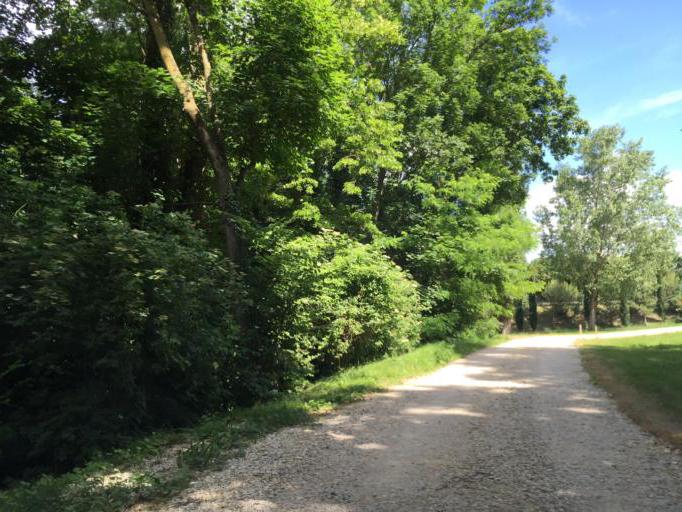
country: FR
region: Rhone-Alpes
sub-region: Departement de la Drome
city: Eurre
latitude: 44.7217
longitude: 4.9822
